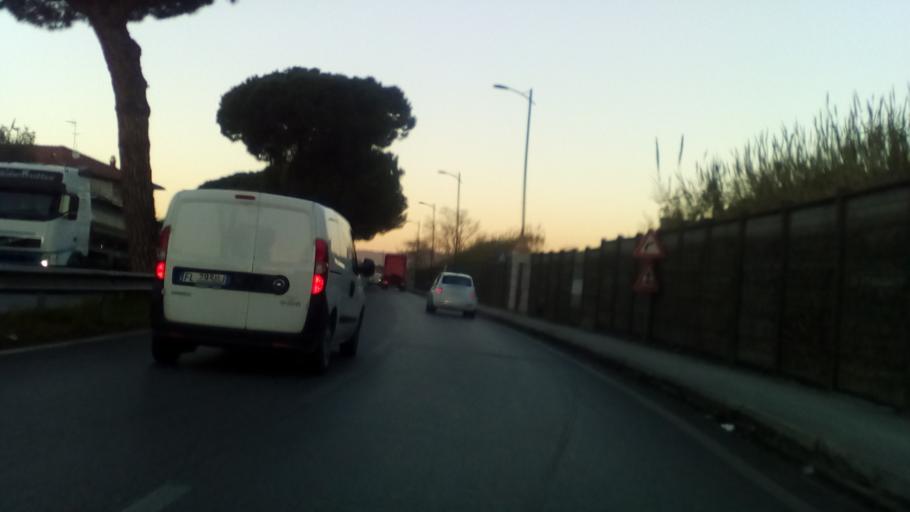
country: IT
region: Tuscany
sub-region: Provincia di Massa-Carrara
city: Massa
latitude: 44.0238
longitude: 10.1039
